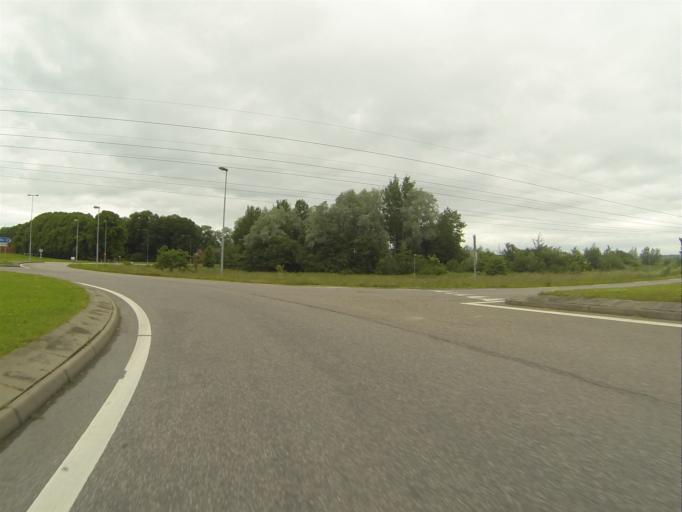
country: SE
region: Skane
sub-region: Staffanstorps Kommun
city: Staffanstorp
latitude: 55.6531
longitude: 13.2027
